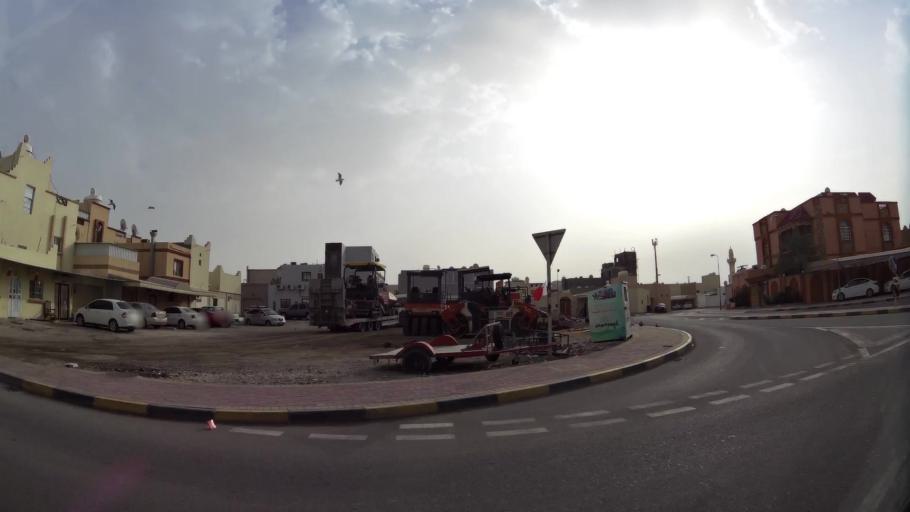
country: BH
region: Northern
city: Ar Rifa'
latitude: 26.1408
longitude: 50.5690
